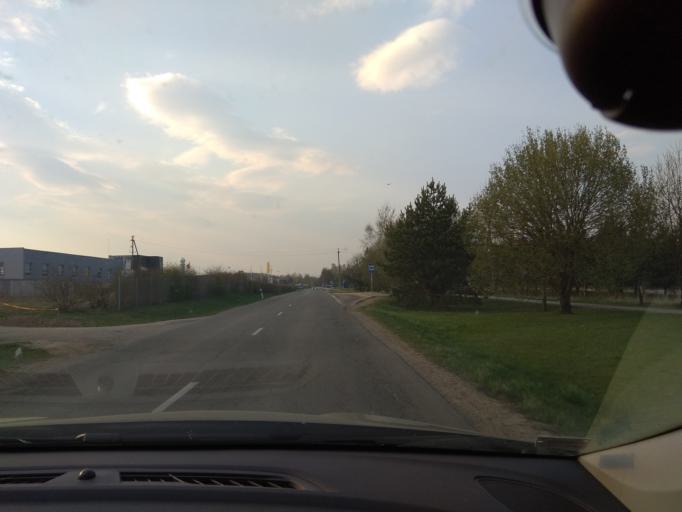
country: LT
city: Grigiskes
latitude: 54.6216
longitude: 25.1132
